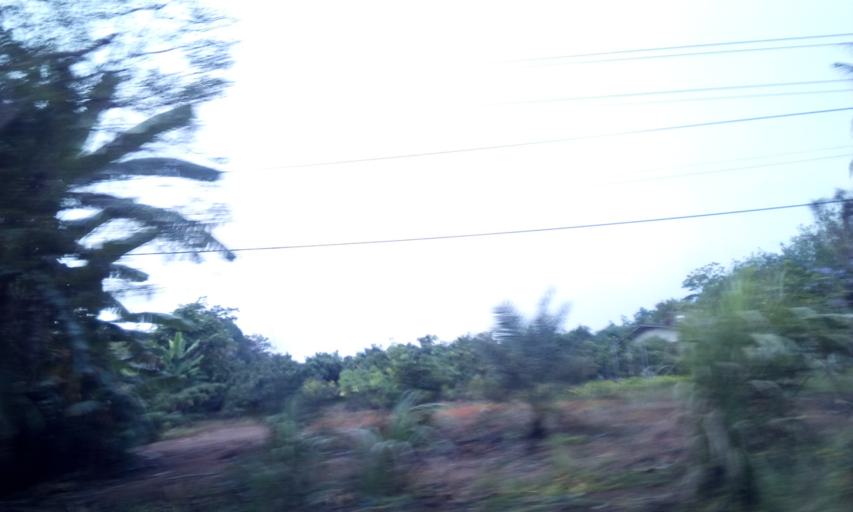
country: TH
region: Trat
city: Khao Saming
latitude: 12.3535
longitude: 102.3810
